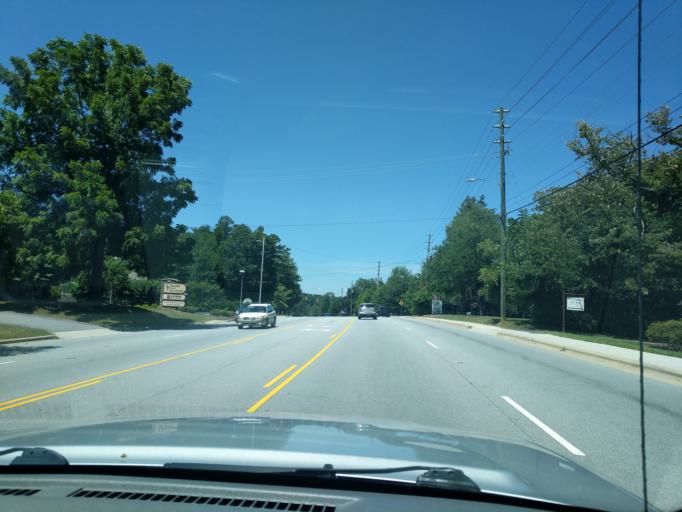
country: US
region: North Carolina
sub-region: Buncombe County
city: Biltmore Forest
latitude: 35.5349
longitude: -82.5281
